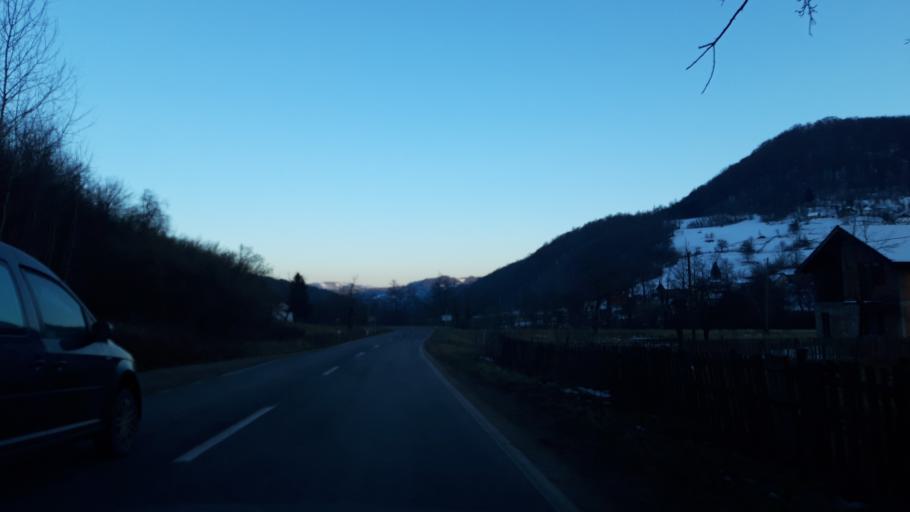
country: BA
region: Republika Srpska
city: Milici
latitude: 44.1699
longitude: 19.0199
